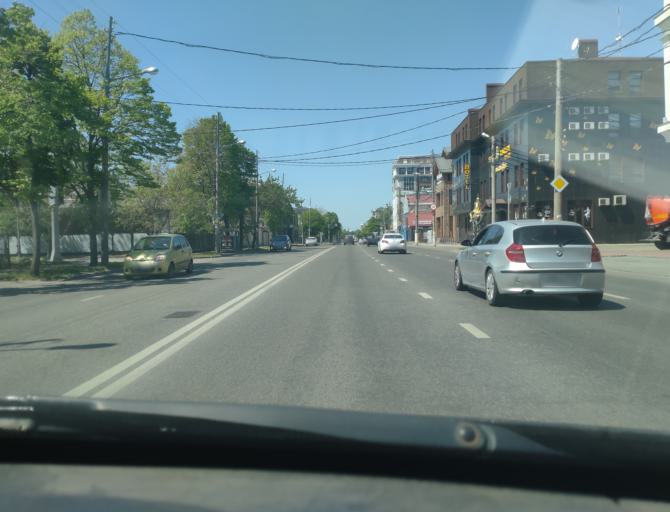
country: RU
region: Krasnodarskiy
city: Krasnodar
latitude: 45.0521
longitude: 38.9512
